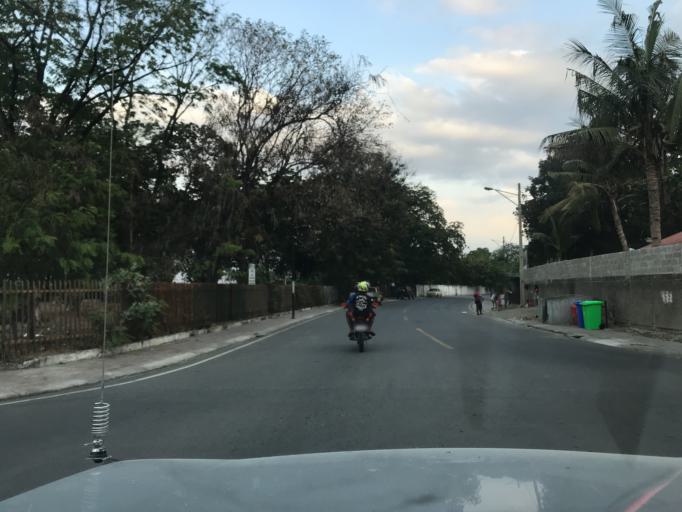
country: TL
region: Dili
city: Dili
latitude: -8.5502
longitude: 125.5682
